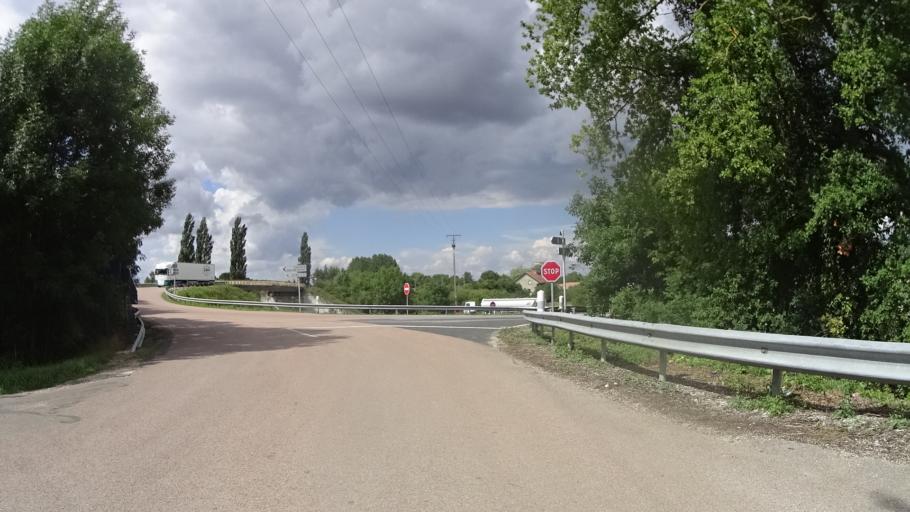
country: FR
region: Champagne-Ardenne
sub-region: Departement de la Haute-Marne
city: Villiers-en-Lieu
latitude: 48.6522
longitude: 4.8286
